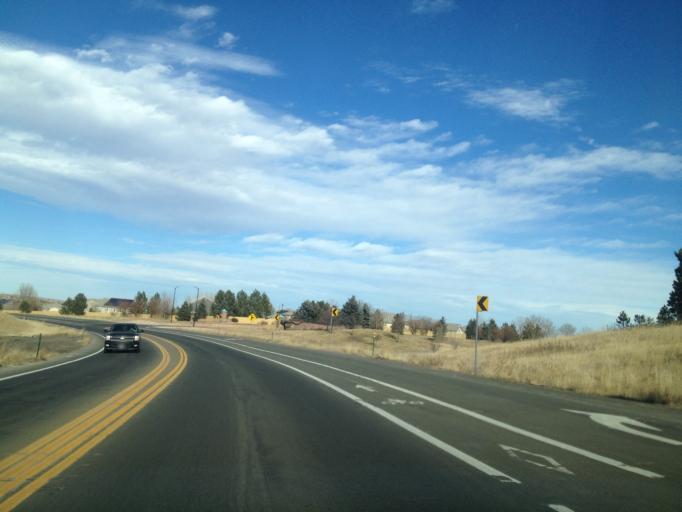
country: US
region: Colorado
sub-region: Boulder County
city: Superior
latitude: 39.9160
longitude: -105.1641
